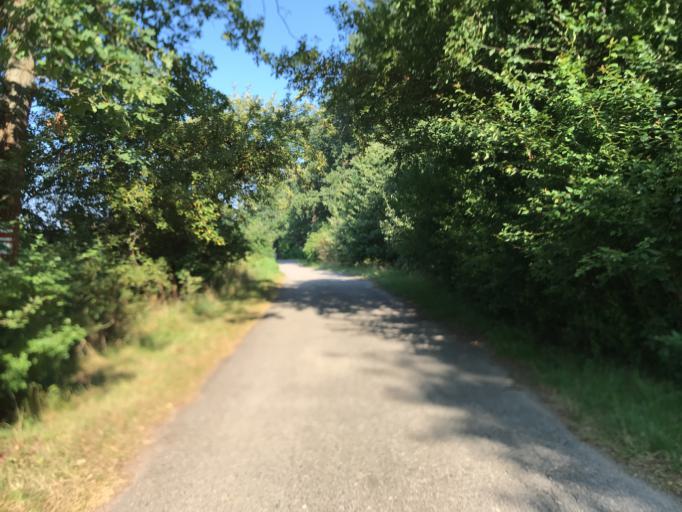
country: CZ
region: Jihocesky
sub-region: Okres Jindrichuv Hradec
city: Trebon
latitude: 48.9920
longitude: 14.7556
